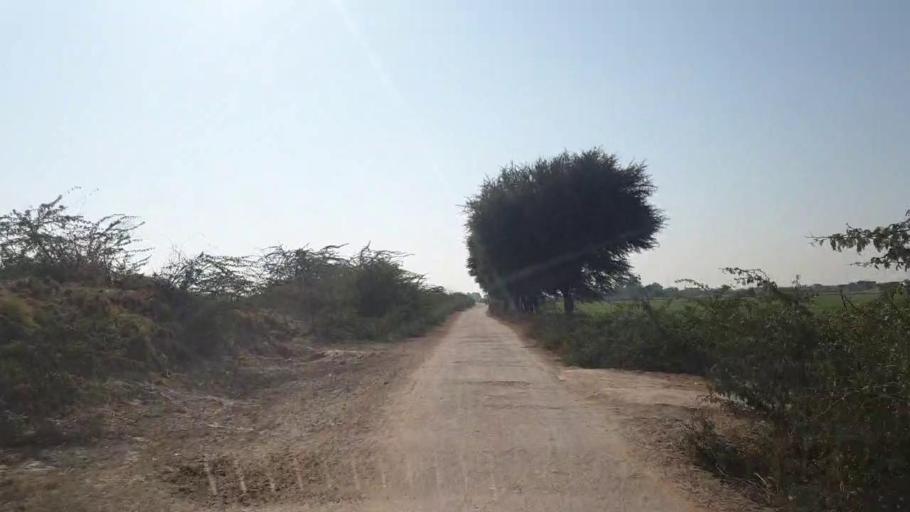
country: PK
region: Sindh
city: Shahpur Chakar
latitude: 26.0840
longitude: 68.6473
